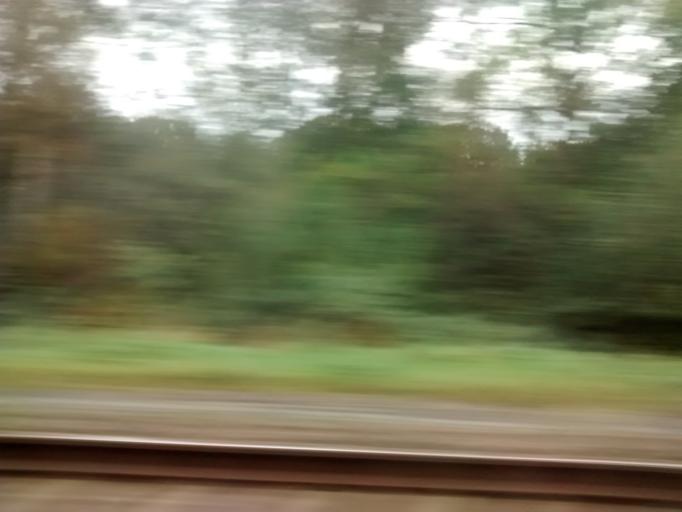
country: NL
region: North Brabant
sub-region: Gemeente Boxtel
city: Boxtel
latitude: 51.6010
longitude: 5.3049
